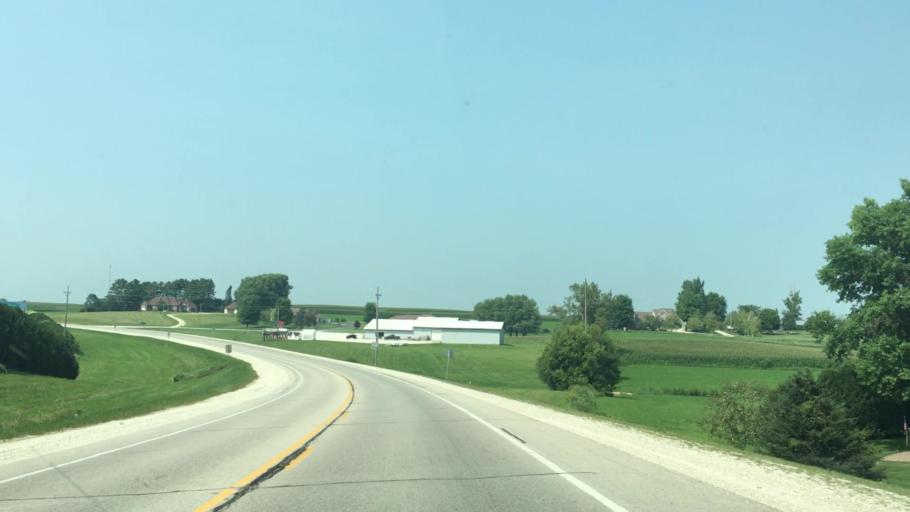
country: US
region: Iowa
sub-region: Winneshiek County
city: Decorah
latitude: 43.1875
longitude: -91.8641
